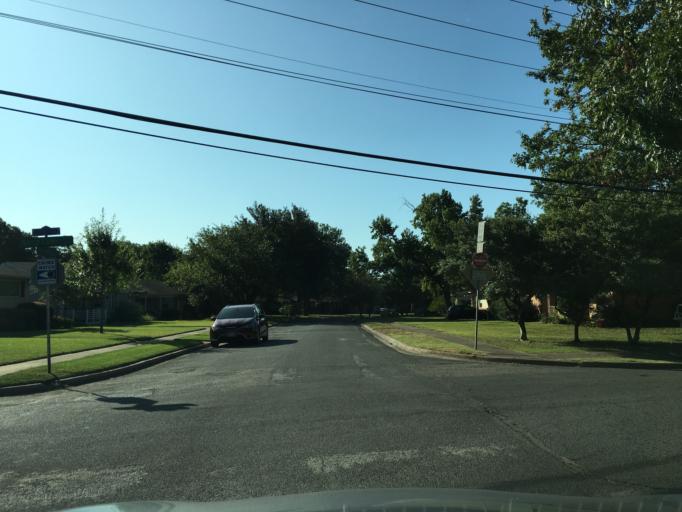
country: US
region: Texas
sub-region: Dallas County
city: Garland
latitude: 32.8582
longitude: -96.7073
